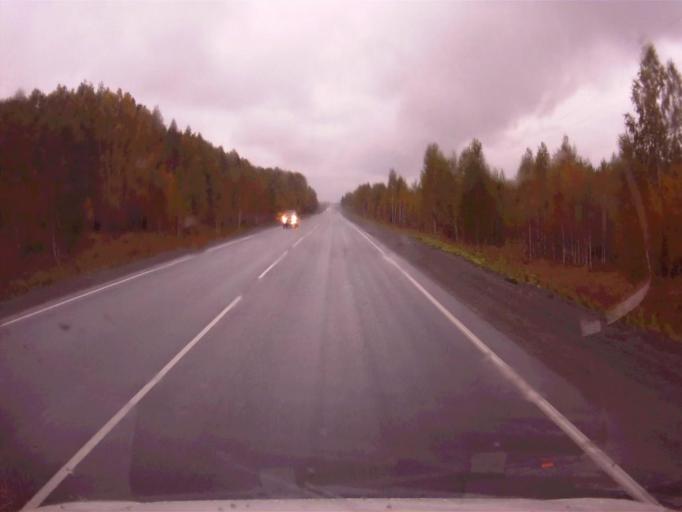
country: RU
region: Chelyabinsk
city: Novogornyy
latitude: 55.4895
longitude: 60.6845
